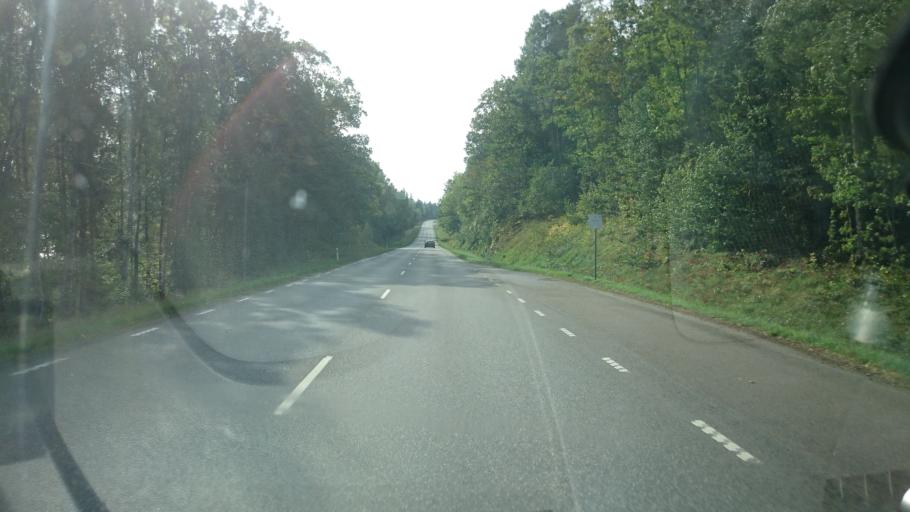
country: SE
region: Vaestra Goetaland
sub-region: Alingsas Kommun
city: Sollebrunn
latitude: 58.0423
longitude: 12.4665
